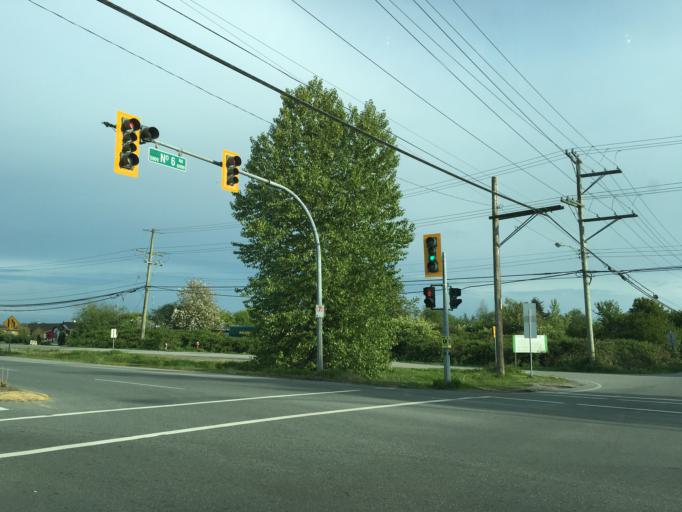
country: CA
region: British Columbia
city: Richmond
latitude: 49.1703
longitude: -123.0692
